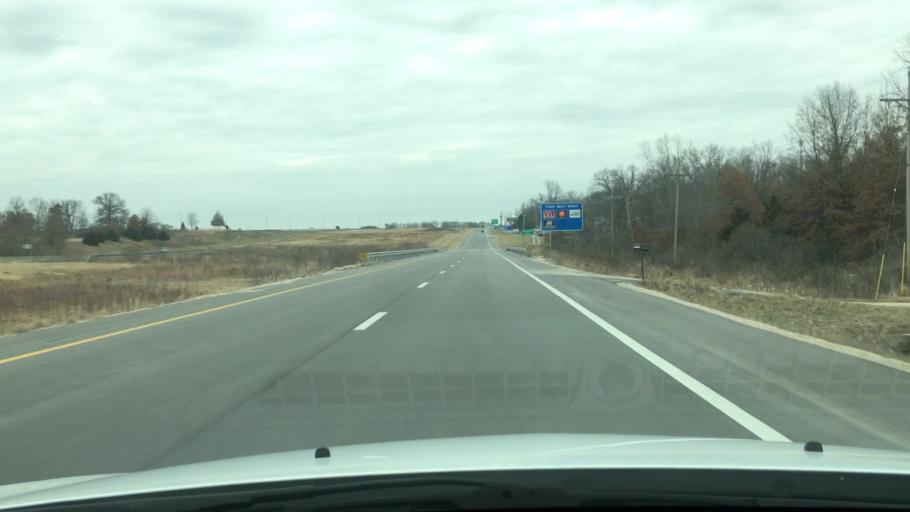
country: US
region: Missouri
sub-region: Audrain County
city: Mexico
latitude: 39.1057
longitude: -91.8958
